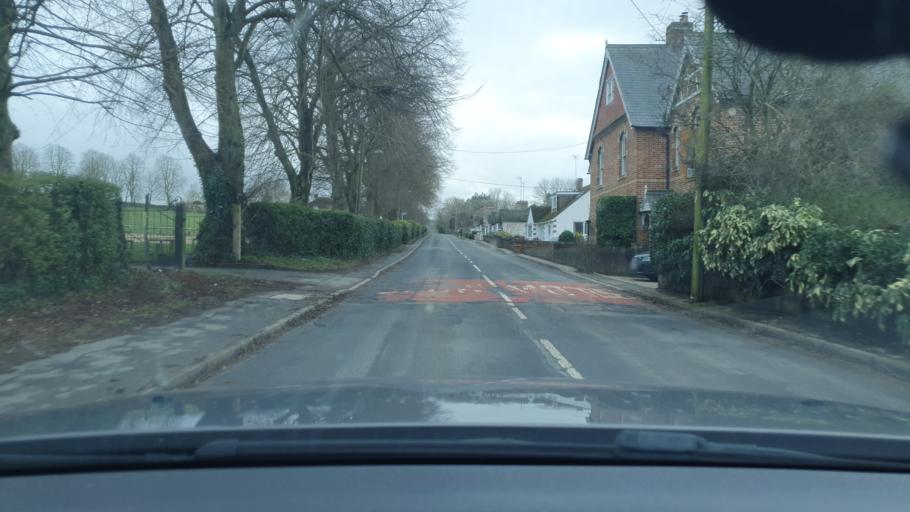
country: GB
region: England
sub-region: Oxfordshire
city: Wantage
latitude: 51.5830
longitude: -1.4274
